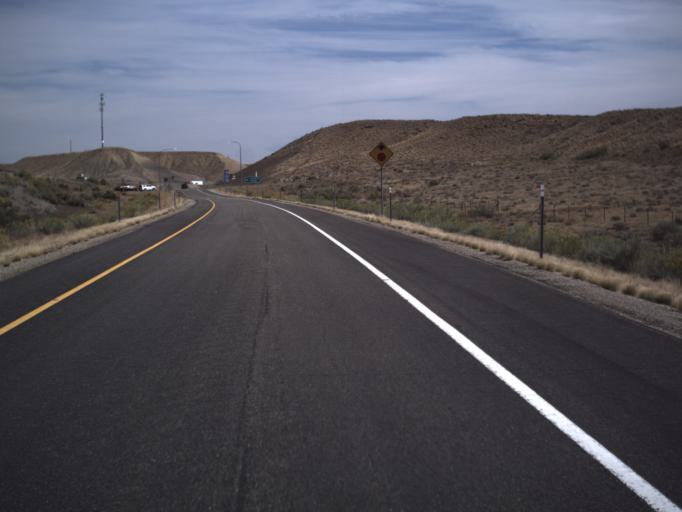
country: US
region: Utah
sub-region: Grand County
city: Moab
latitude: 38.9604
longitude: -109.7264
